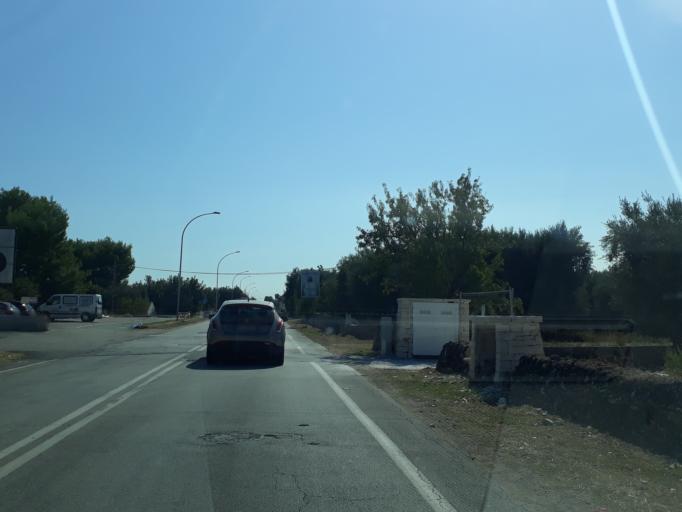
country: IT
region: Apulia
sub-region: Provincia di Bari
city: Monopoli
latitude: 40.9367
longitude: 17.3087
